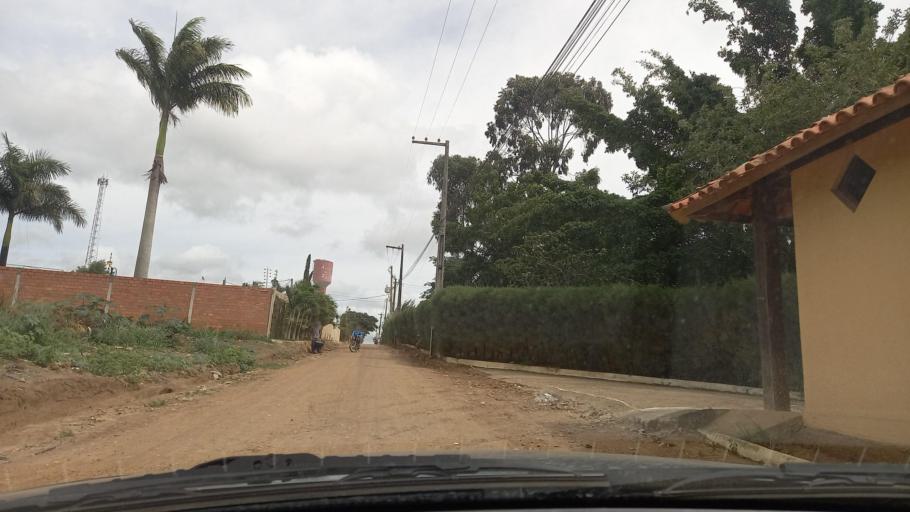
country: BR
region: Pernambuco
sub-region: Gravata
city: Gravata
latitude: -8.1917
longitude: -35.5894
